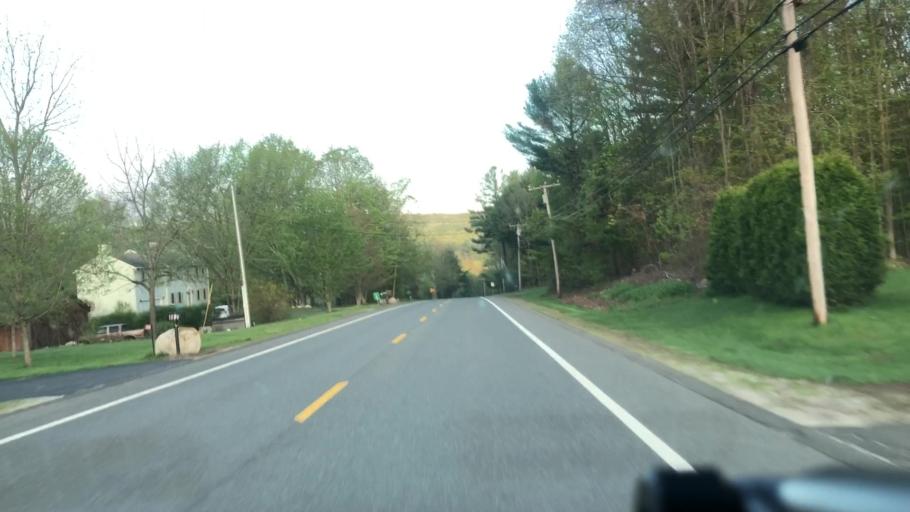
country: US
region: Massachusetts
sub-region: Hampshire County
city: Westhampton
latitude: 42.2871
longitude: -72.7661
